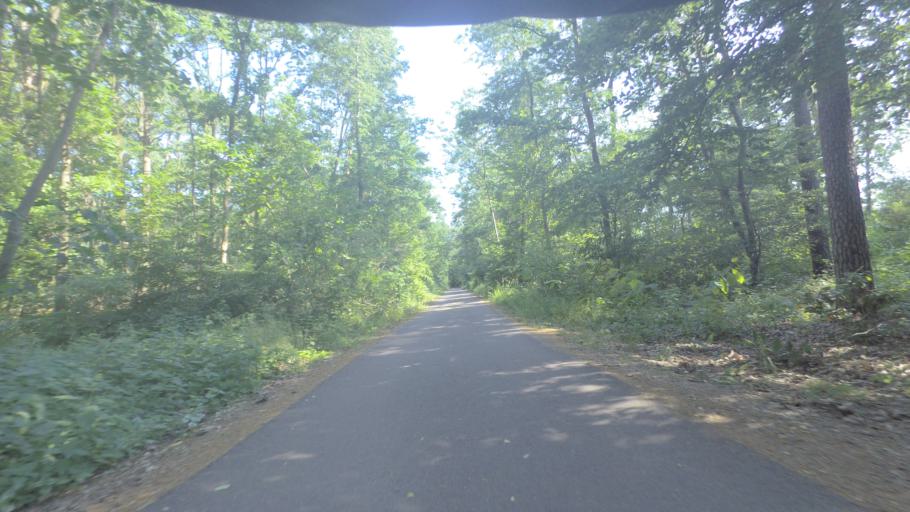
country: DE
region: Saxony-Anhalt
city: Rodleben
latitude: 51.8392
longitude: 12.1685
